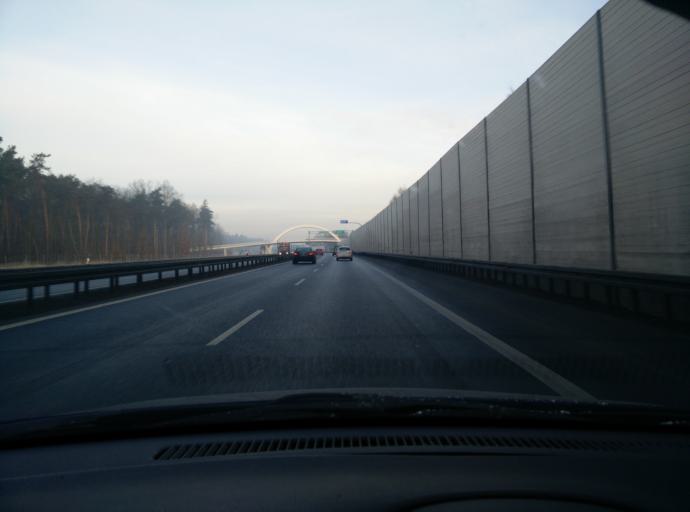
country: PL
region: Greater Poland Voivodeship
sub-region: Powiat poznanski
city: Kornik
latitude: 52.2932
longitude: 17.0540
